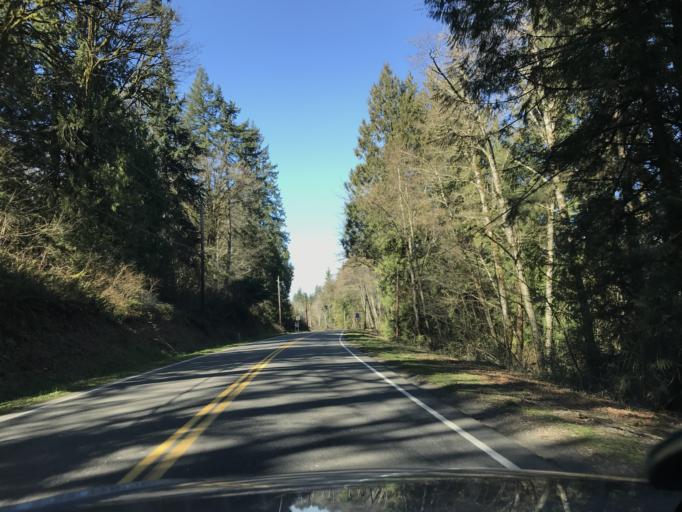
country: US
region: Washington
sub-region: Pierce County
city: Canterwood
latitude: 47.3507
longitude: -122.6074
